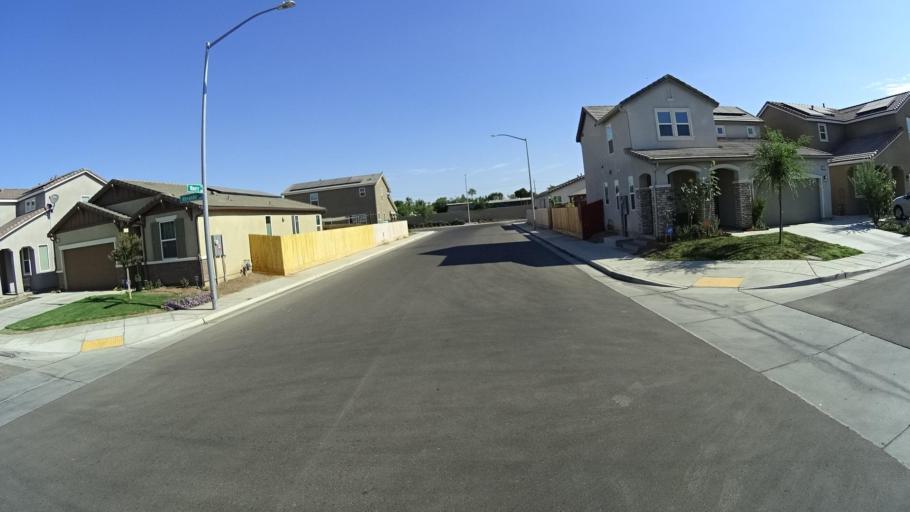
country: US
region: California
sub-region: Fresno County
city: Sunnyside
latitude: 36.7154
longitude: -119.7322
